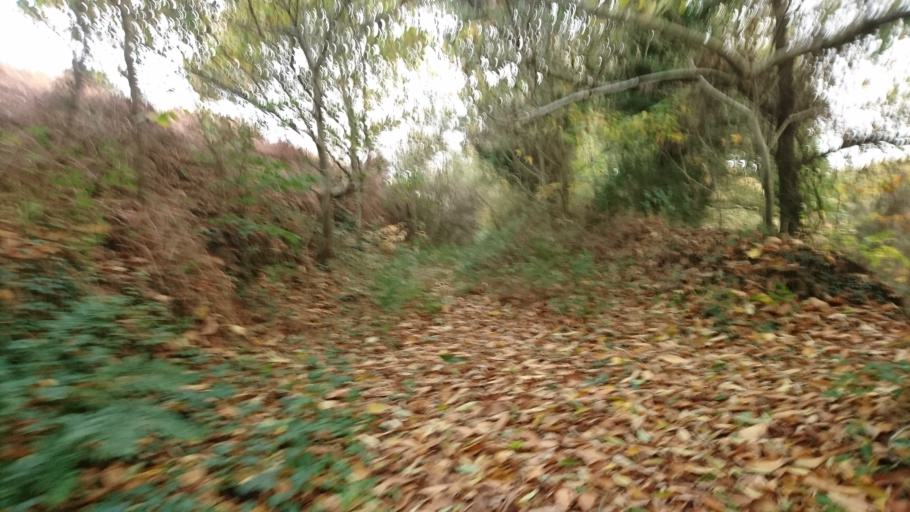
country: FR
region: Brittany
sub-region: Departement du Finistere
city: Lampaul-Plouarzel
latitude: 48.4360
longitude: -4.7669
